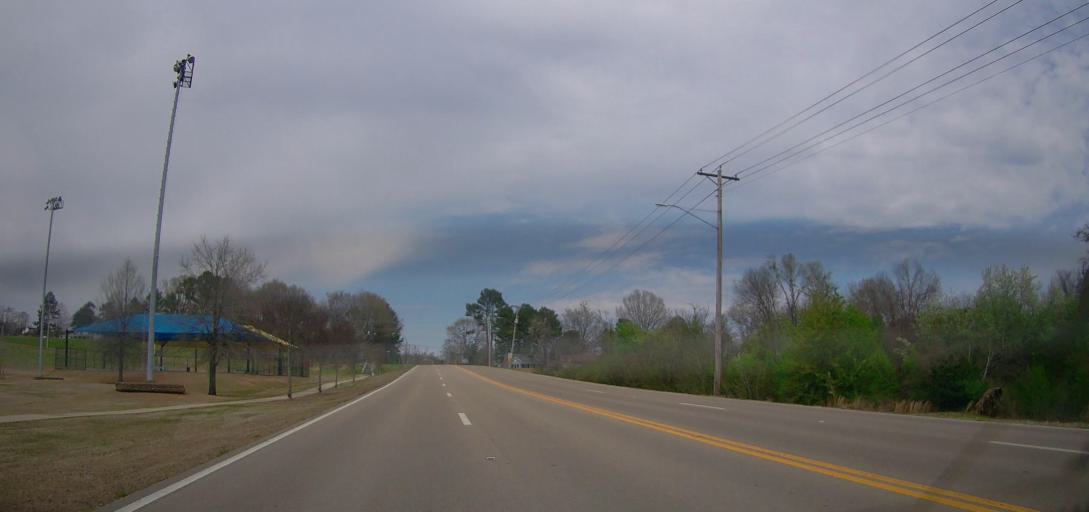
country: US
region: Mississippi
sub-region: Lee County
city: Tupelo
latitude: 34.2679
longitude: -88.7035
